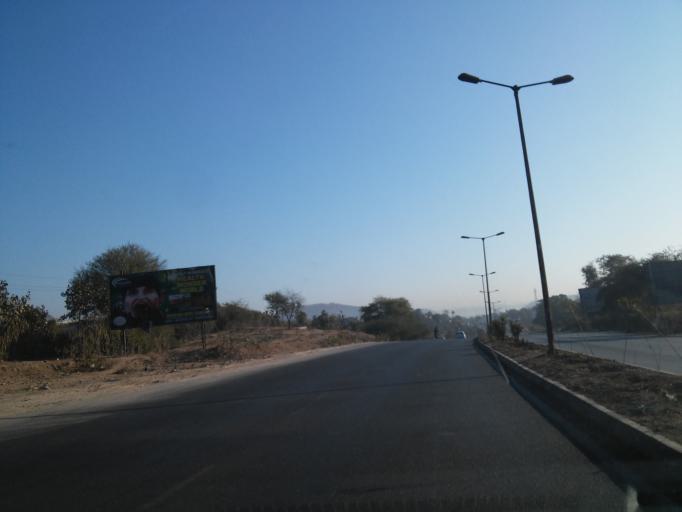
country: IN
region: Rajasthan
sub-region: Dungarpur
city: Dungarpur
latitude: 23.9959
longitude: 73.6317
